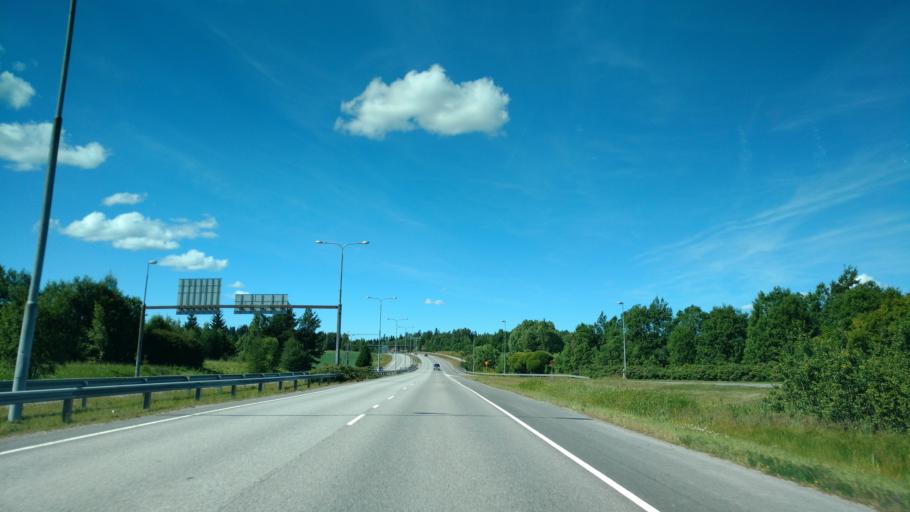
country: FI
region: Varsinais-Suomi
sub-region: Turku
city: Turku
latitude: 60.4875
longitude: 22.3193
